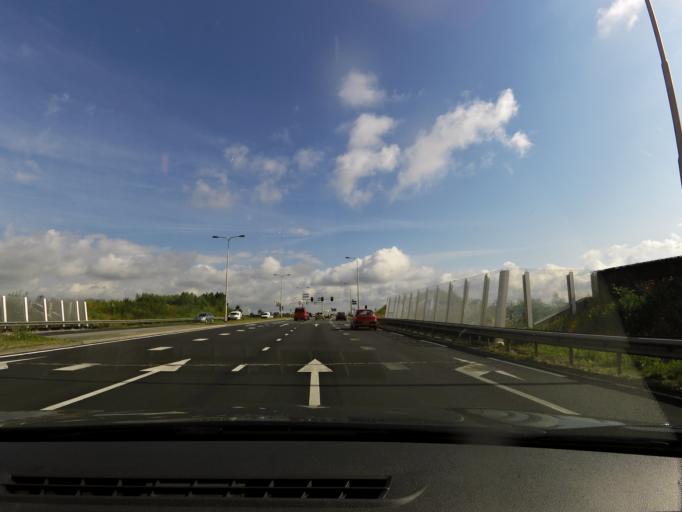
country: NL
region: Utrecht
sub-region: Gemeente Veenendaal
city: Veenendaal
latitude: 52.0343
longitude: 5.5807
